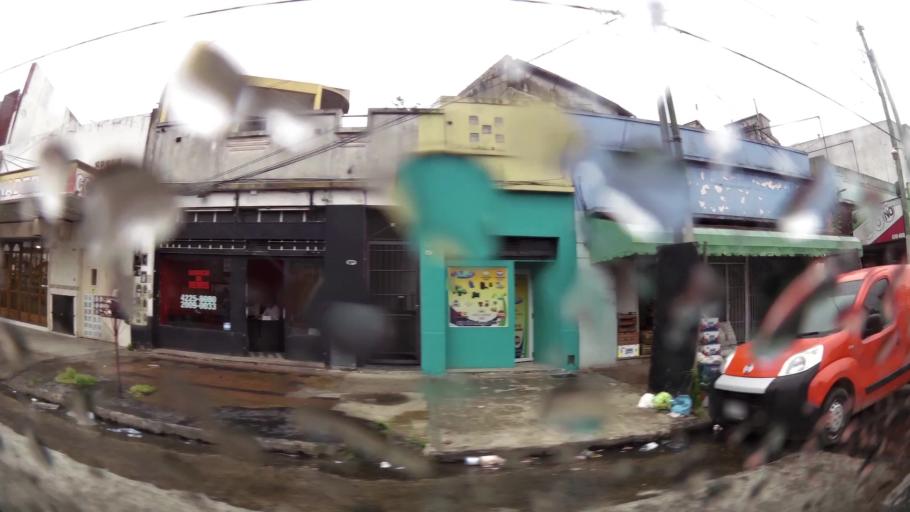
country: AR
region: Buenos Aires
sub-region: Partido de Lanus
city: Lanus
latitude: -34.7068
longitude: -58.4015
